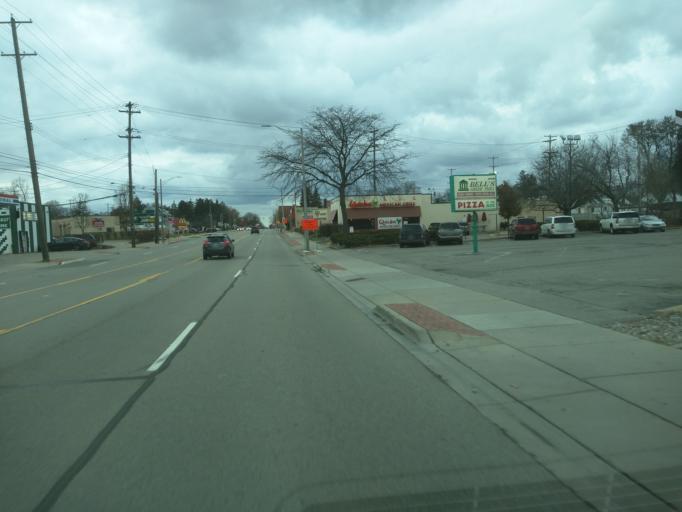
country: US
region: Michigan
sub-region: Ingham County
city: East Lansing
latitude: 42.7310
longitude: -84.4679
